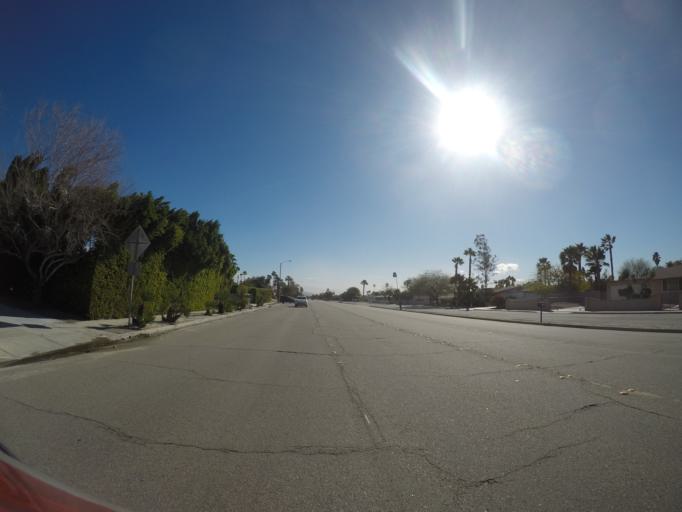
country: US
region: California
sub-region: Riverside County
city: Palm Springs
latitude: 33.8522
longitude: -116.5355
